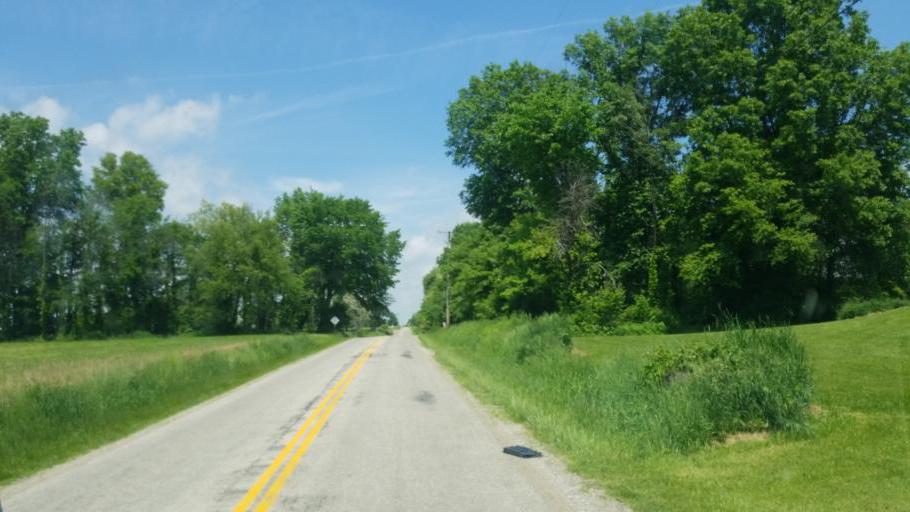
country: US
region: Ohio
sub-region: Ashland County
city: Ashland
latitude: 40.8358
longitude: -82.1748
